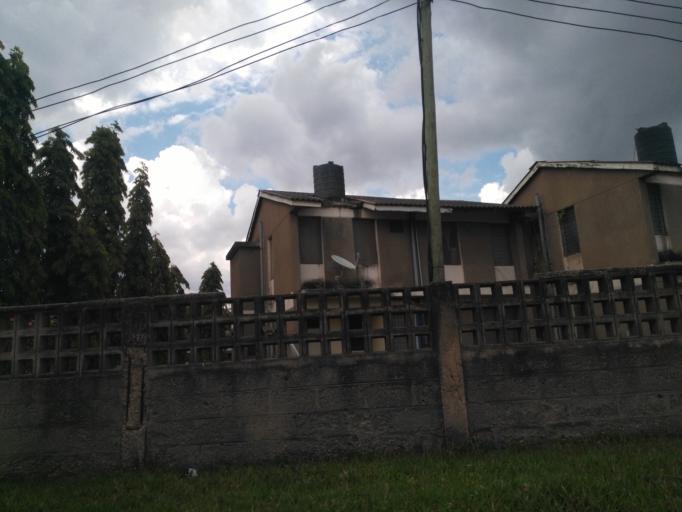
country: TZ
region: Dar es Salaam
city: Magomeni
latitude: -6.7563
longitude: 39.2395
